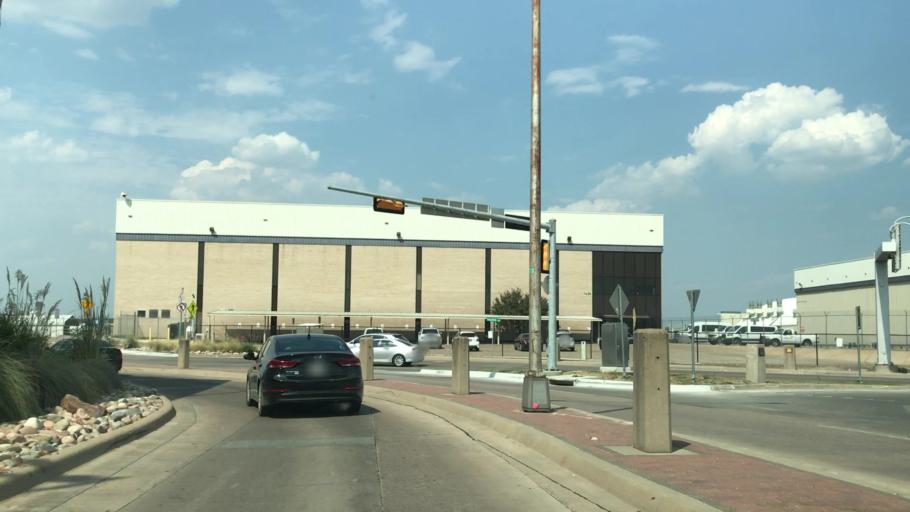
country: US
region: Texas
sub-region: Dallas County
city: University Park
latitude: 32.8405
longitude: -96.8462
